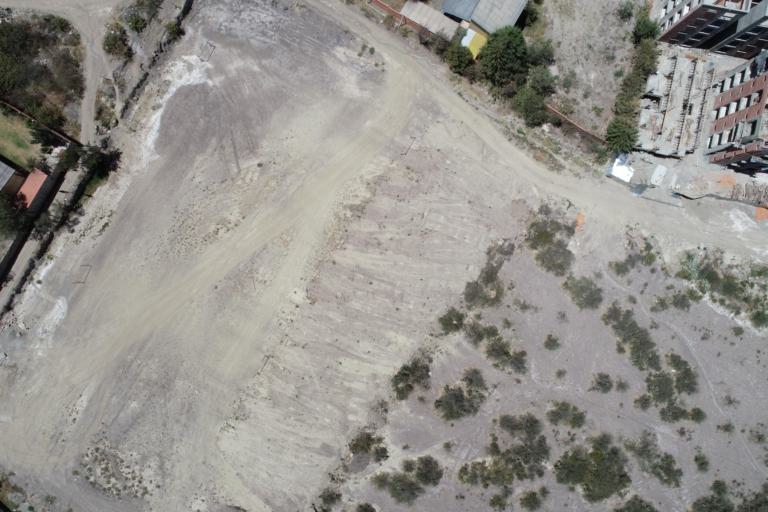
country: BO
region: La Paz
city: La Paz
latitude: -16.6457
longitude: -68.0416
